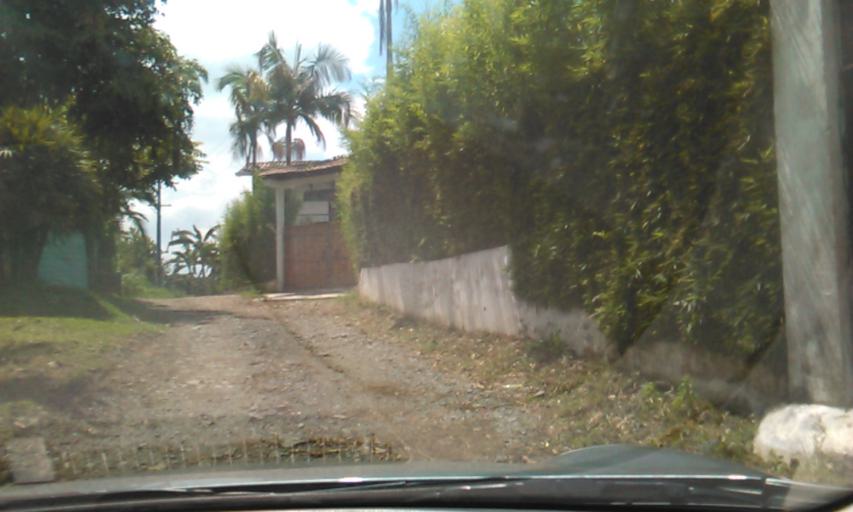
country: CO
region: Quindio
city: Circasia
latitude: 4.5937
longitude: -75.6503
